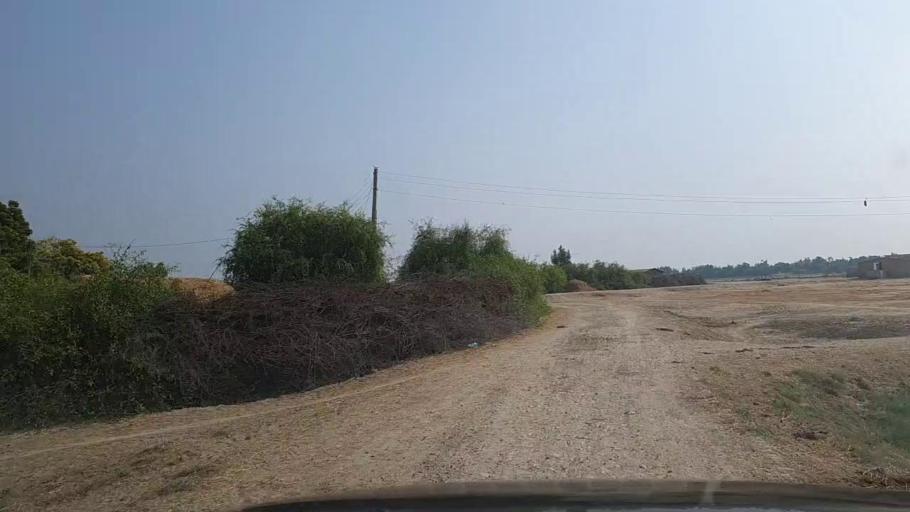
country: PK
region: Sindh
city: Mirpur Batoro
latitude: 24.6861
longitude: 68.2217
